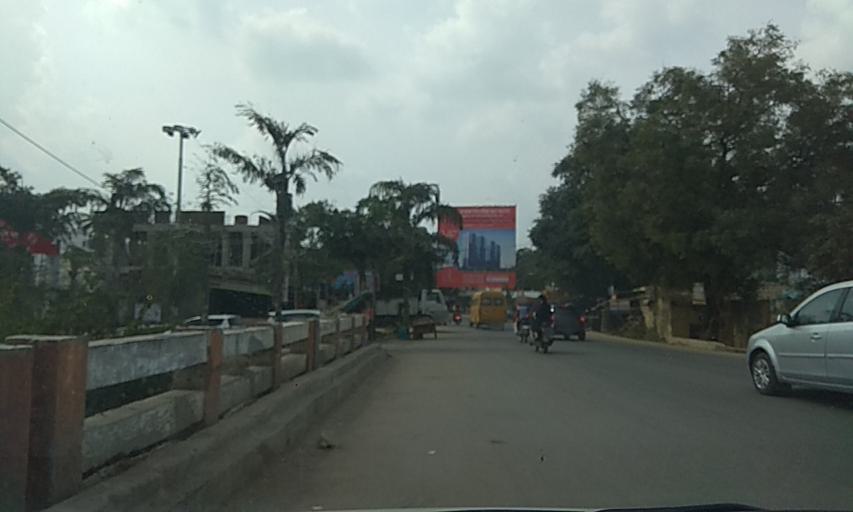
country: IN
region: Maharashtra
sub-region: Pune Division
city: Pimpri
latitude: 18.5752
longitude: 73.7090
